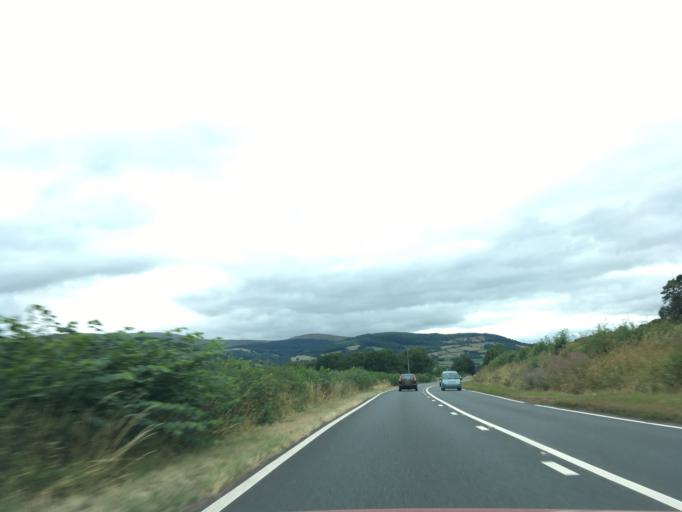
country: GB
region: Wales
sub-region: Blaenau Gwent
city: Brynmawr
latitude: 51.8928
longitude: -3.2542
